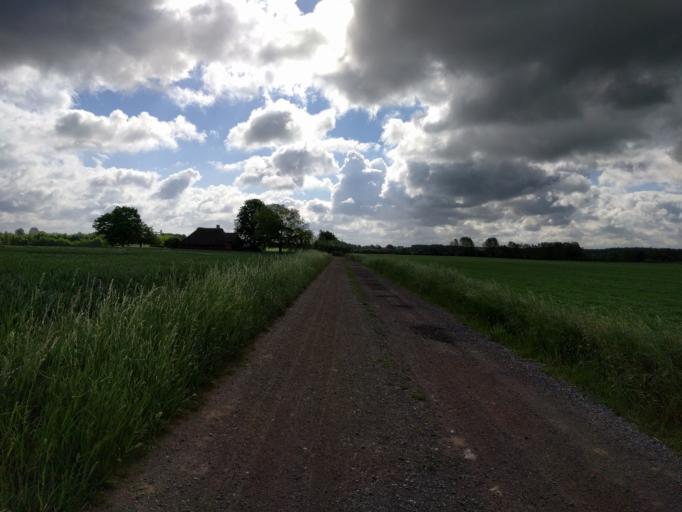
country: DK
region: South Denmark
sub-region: Kerteminde Kommune
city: Kerteminde
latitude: 55.4204
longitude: 10.6306
